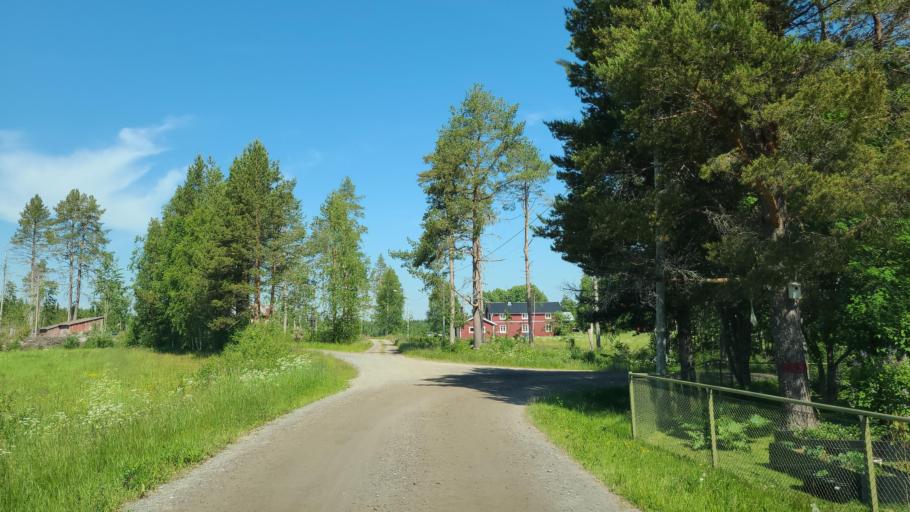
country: SE
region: Vaesterbotten
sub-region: Robertsfors Kommun
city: Robertsfors
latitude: 64.0866
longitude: 20.8416
